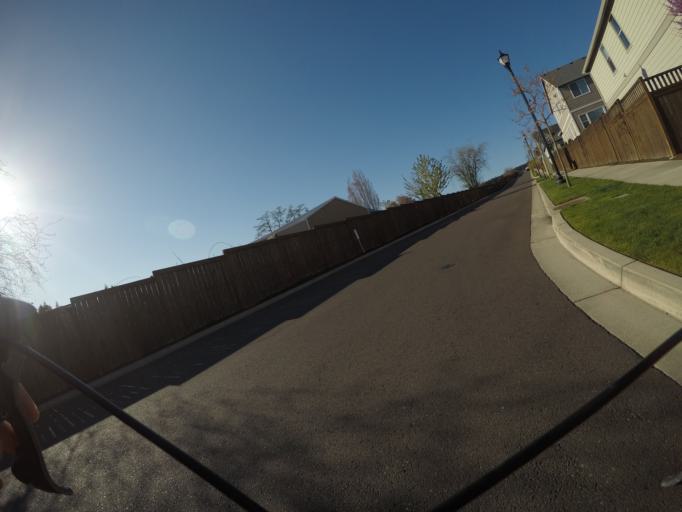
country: US
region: Oregon
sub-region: Washington County
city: King City
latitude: 45.4237
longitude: -122.8568
